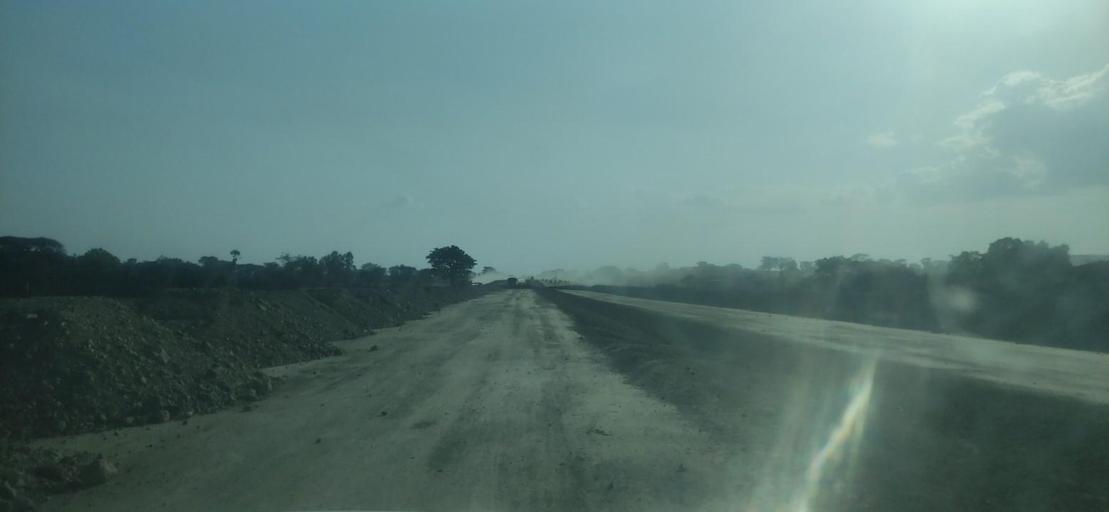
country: ET
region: Southern Nations, Nationalities, and People's Region
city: Hawassa
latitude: 7.1590
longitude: 38.4820
